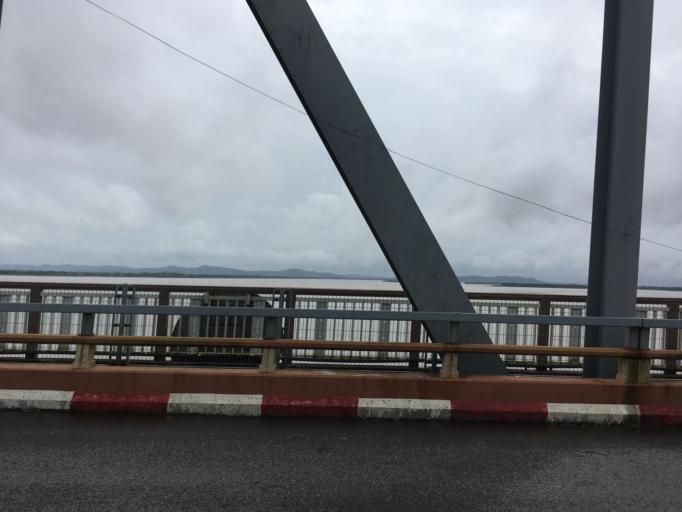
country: MM
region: Mon
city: Mawlamyine
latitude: 16.5083
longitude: 97.6192
